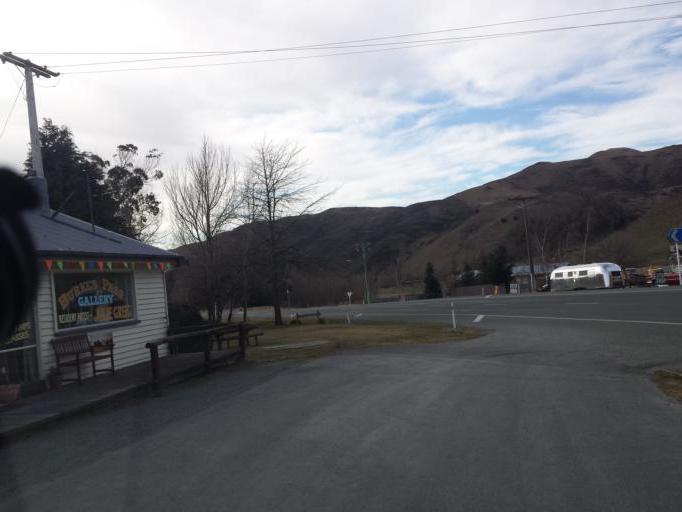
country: NZ
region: Canterbury
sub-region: Timaru District
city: Pleasant Point
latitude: -44.0895
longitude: 170.6521
